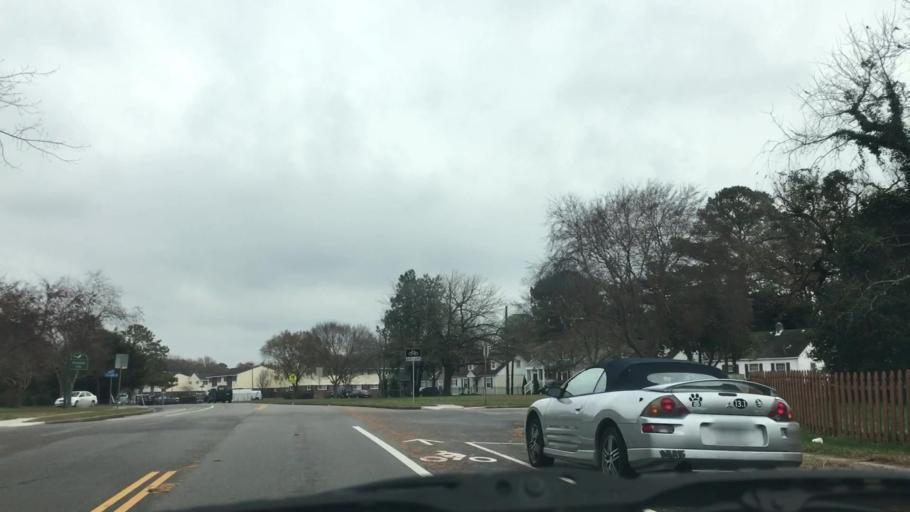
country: US
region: Virginia
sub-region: City of Norfolk
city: Norfolk
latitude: 36.8759
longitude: -76.2408
